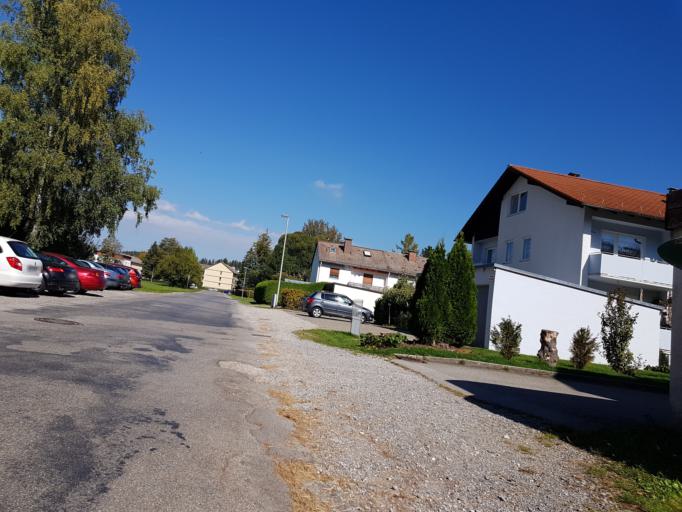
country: DE
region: Bavaria
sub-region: Swabia
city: Fuessen
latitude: 47.5684
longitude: 10.6864
